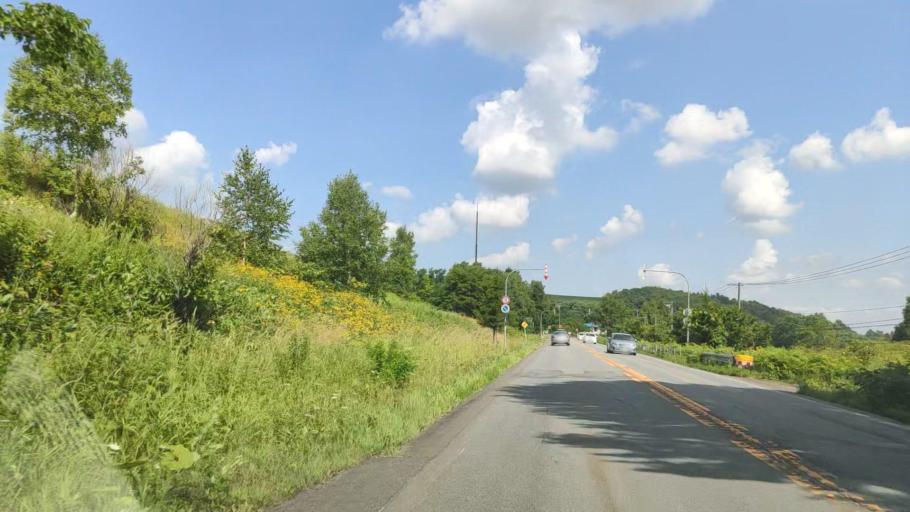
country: JP
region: Hokkaido
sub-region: Asahikawa-shi
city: Asahikawa
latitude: 43.5630
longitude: 142.4348
